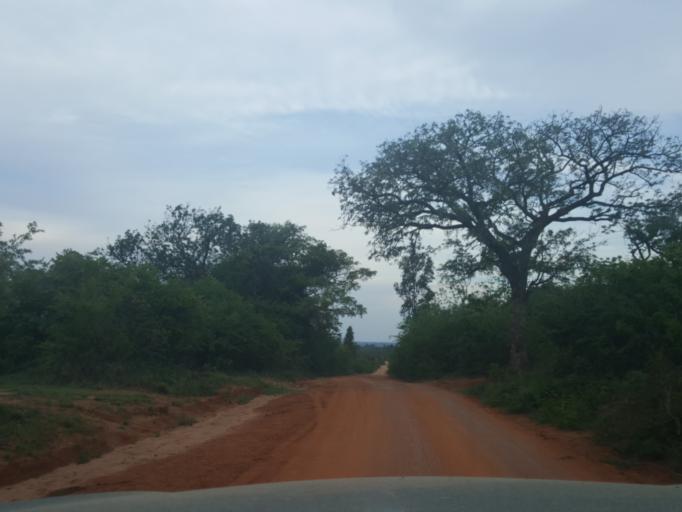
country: ZA
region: Limpopo
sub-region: Mopani District Municipality
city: Hoedspruit
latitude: -24.5880
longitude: 30.9584
